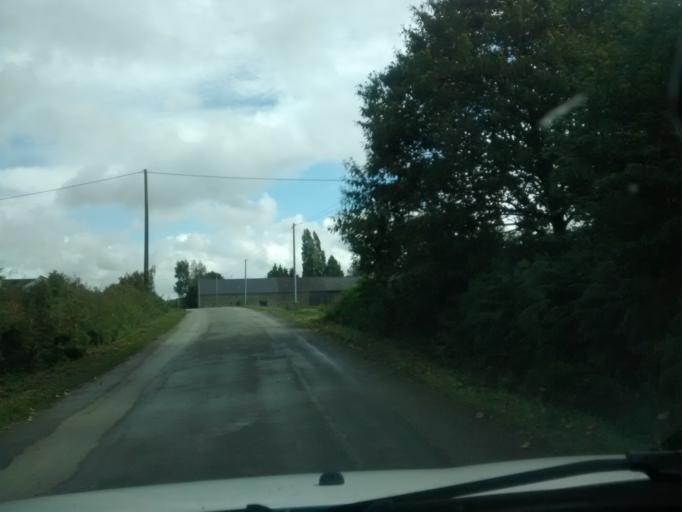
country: FR
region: Brittany
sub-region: Departement d'Ille-et-Vilaine
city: Chateaubourg
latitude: 48.1256
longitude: -1.3971
